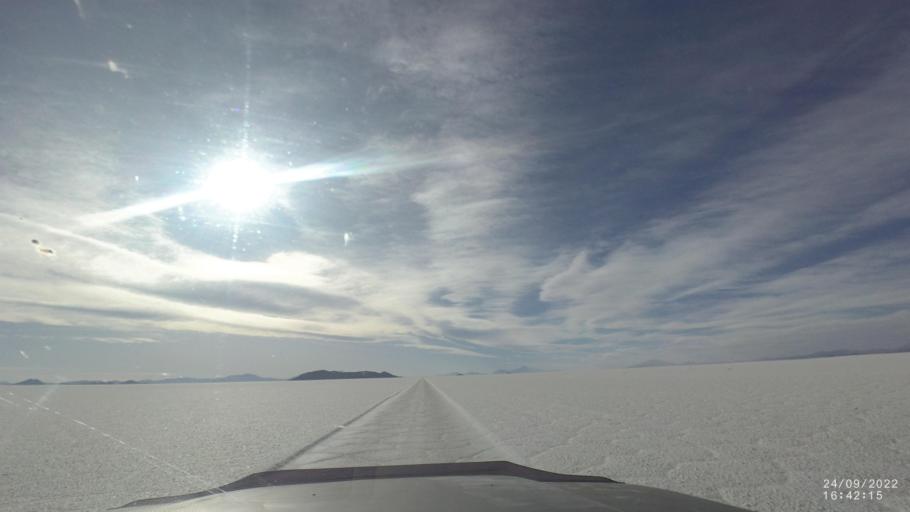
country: BO
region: Potosi
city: Colchani
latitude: -20.1769
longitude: -67.7290
